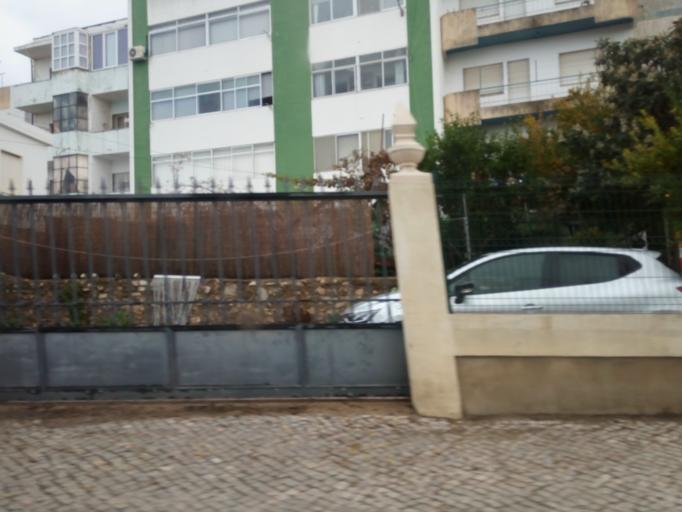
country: PT
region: Faro
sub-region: Loule
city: Loule
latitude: 37.1347
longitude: -8.0209
